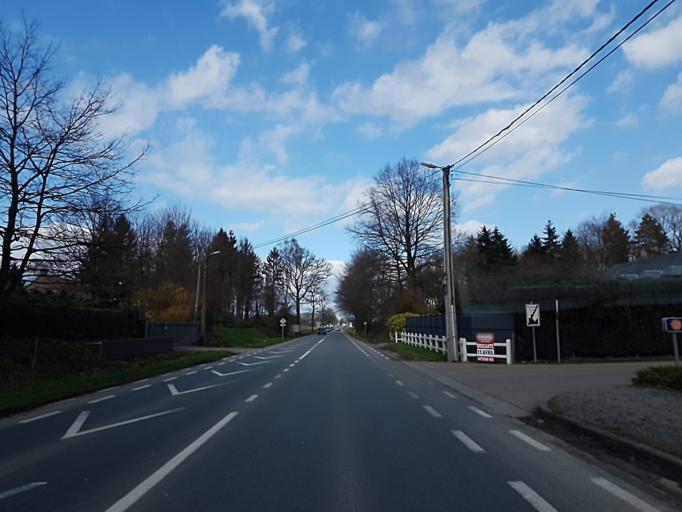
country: BE
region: Wallonia
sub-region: Province du Brabant Wallon
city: Perwez
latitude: 50.6385
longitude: 4.7826
